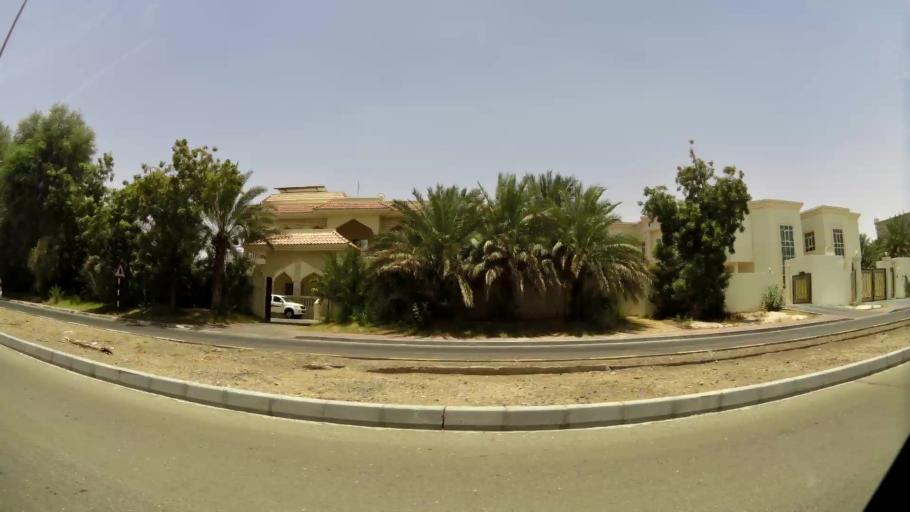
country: OM
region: Al Buraimi
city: Al Buraymi
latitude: 24.2632
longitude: 55.7308
